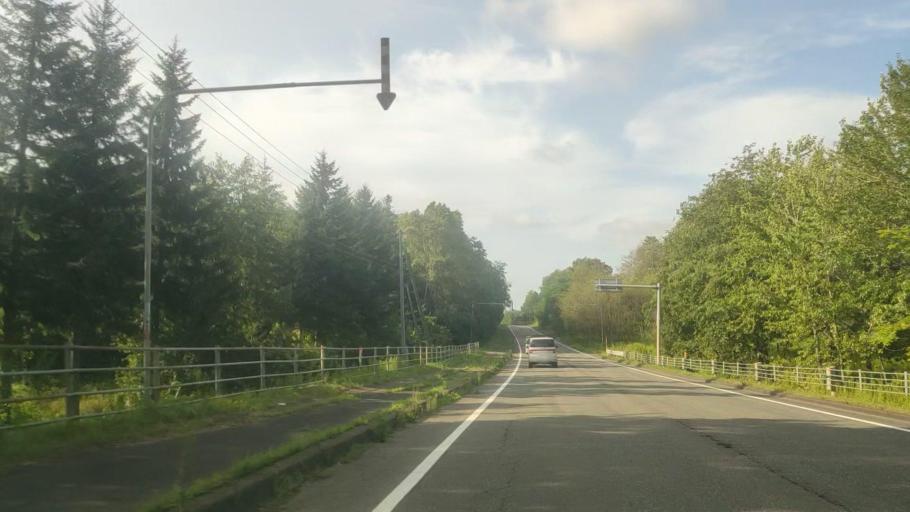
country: JP
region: Hokkaido
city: Chitose
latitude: 42.8679
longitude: 141.8226
